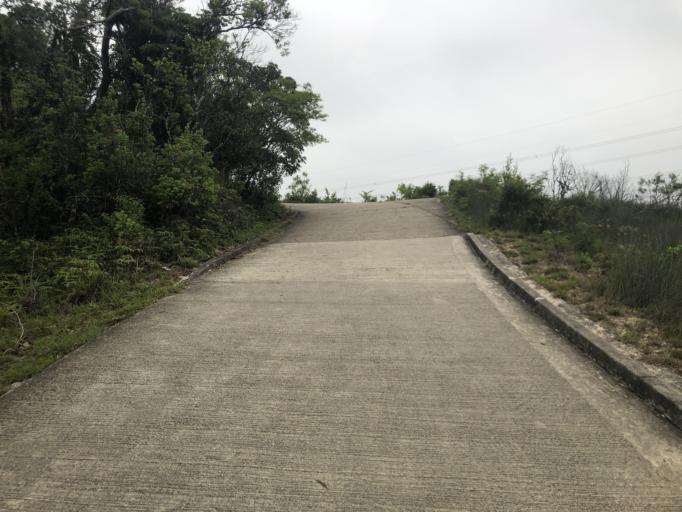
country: HK
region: Sha Tin
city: Sha Tin
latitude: 22.3923
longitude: 114.1649
